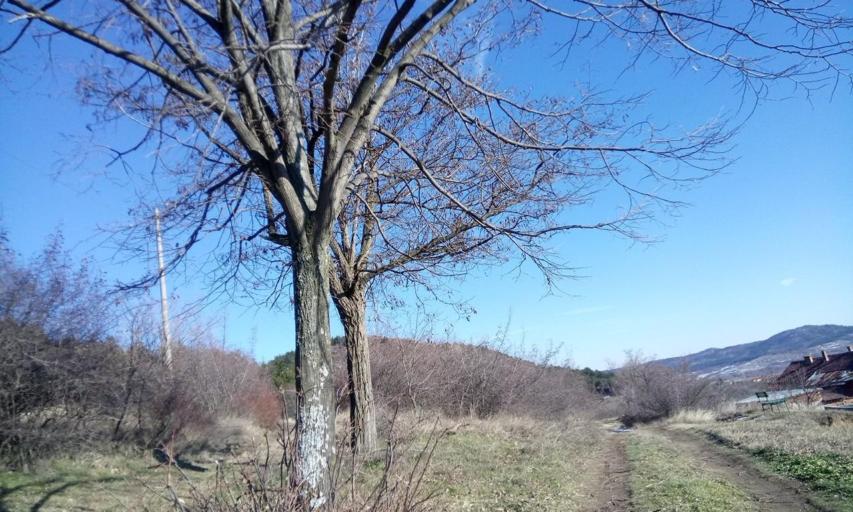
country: BG
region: Plovdiv
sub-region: Obshtina Khisarya
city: Khisarya
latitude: 42.5255
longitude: 24.7167
